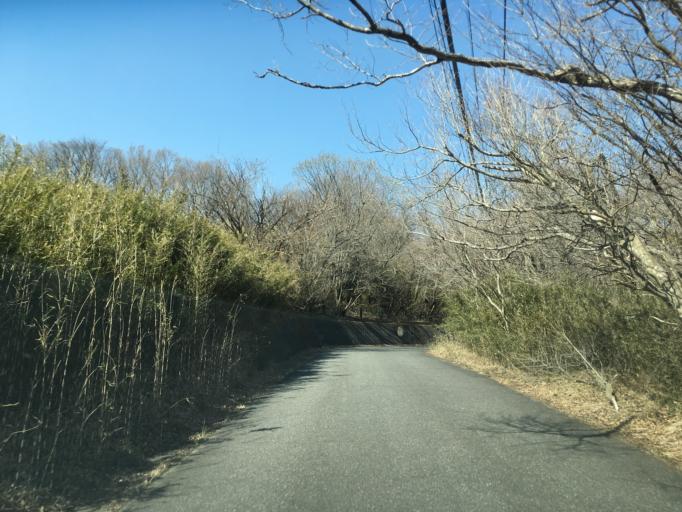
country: JP
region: Tochigi
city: Kuroiso
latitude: 37.0694
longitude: 140.0030
